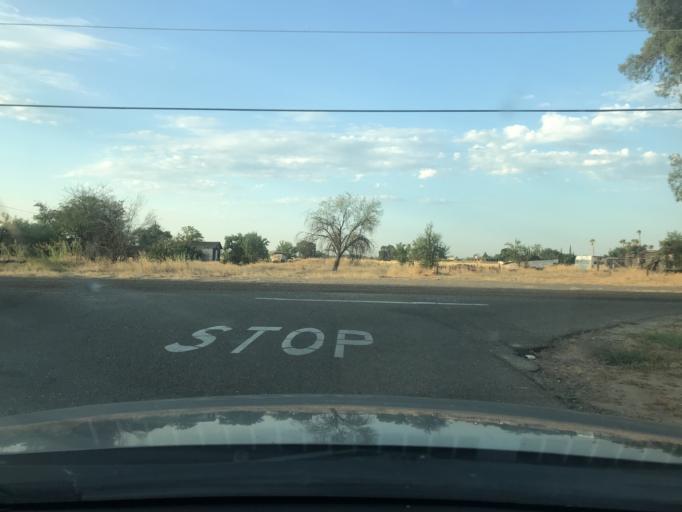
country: US
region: California
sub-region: Merced County
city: Merced
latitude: 37.3247
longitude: -120.5379
